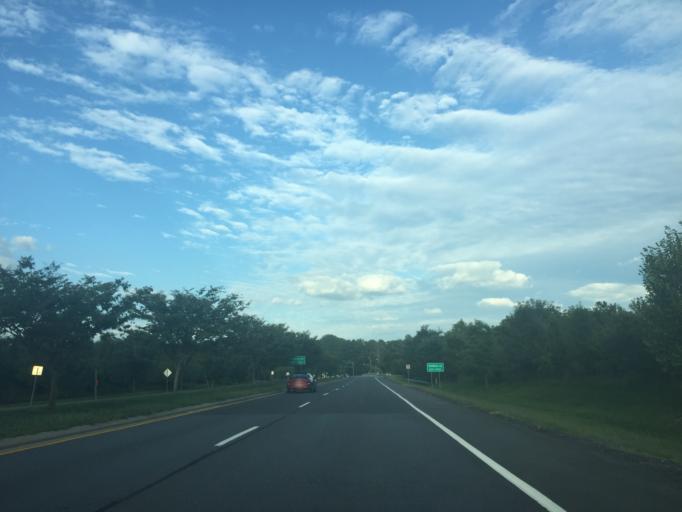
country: US
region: Maryland
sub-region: Montgomery County
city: Cloverly
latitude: 39.1185
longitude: -77.0251
